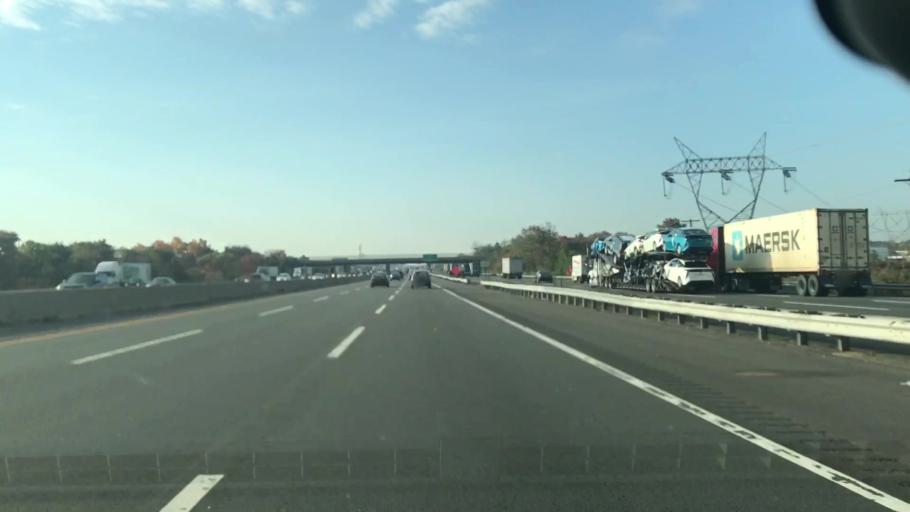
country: US
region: New Jersey
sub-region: Middlesex County
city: Jamesburg
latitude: 40.3779
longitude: -74.4634
